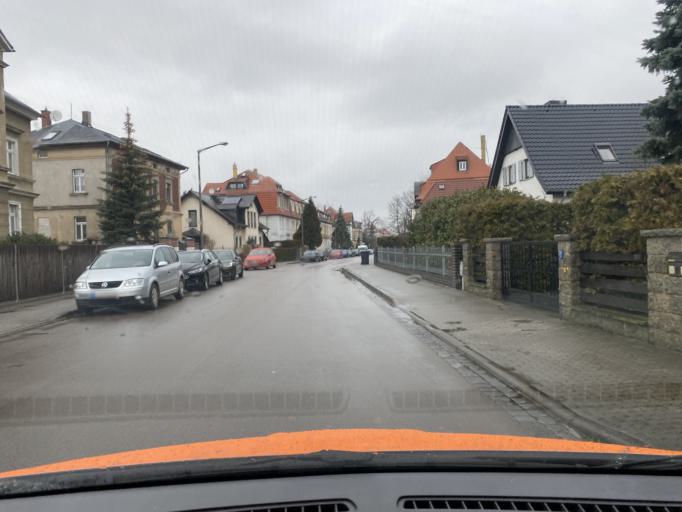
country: DE
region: Saxony
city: Markkleeberg
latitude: 51.2766
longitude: 12.3112
